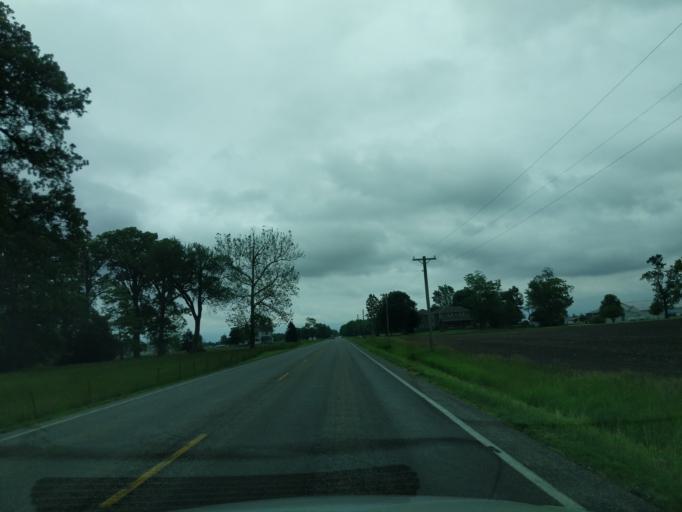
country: US
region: Indiana
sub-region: Tipton County
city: Tipton
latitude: 40.2833
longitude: -85.9779
